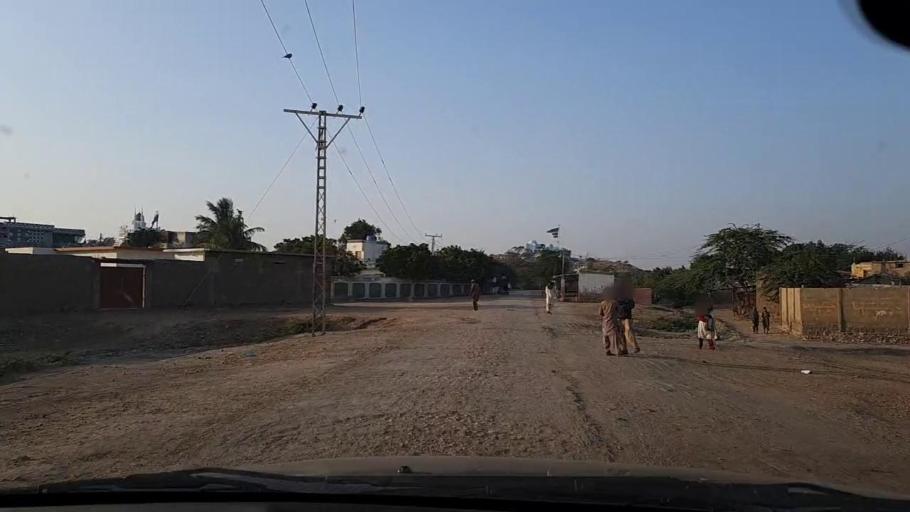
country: PK
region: Sindh
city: Thatta
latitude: 24.5578
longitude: 67.8816
